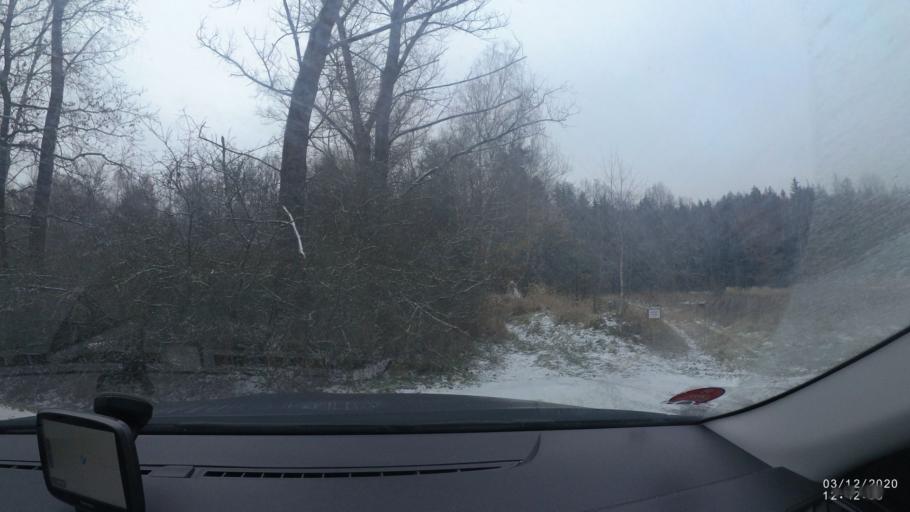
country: CZ
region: Central Bohemia
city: Revnicov
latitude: 50.1647
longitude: 13.8408
